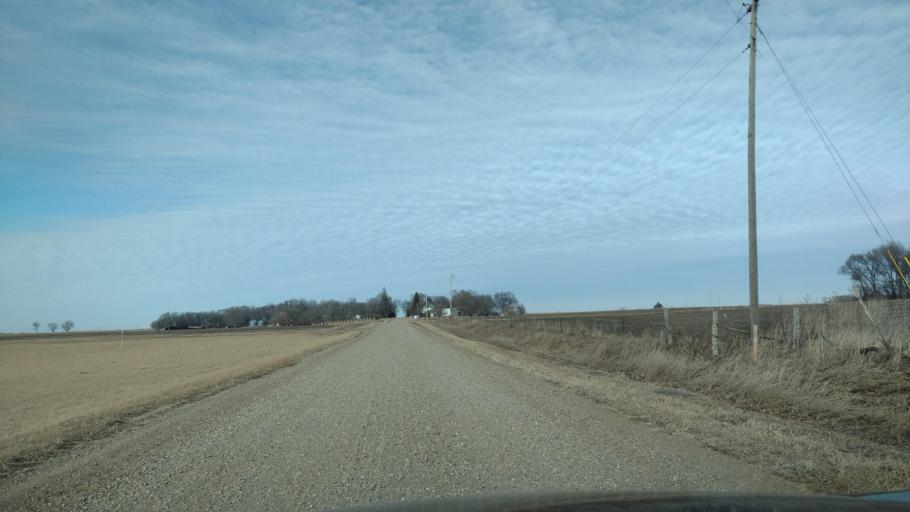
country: US
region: South Dakota
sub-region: Union County
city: Beresford
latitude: 42.9570
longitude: -96.8055
